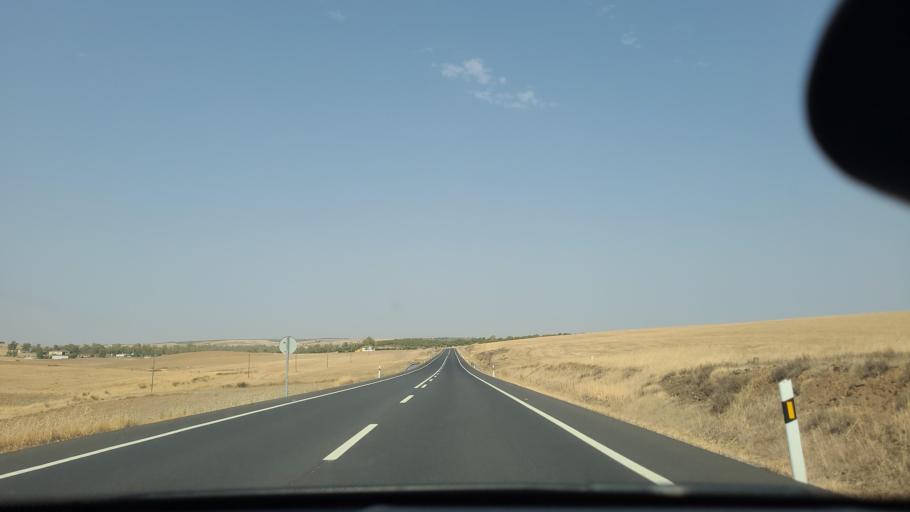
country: ES
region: Extremadura
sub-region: Provincia de Badajoz
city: Berlanga
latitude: 38.2711
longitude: -5.7963
